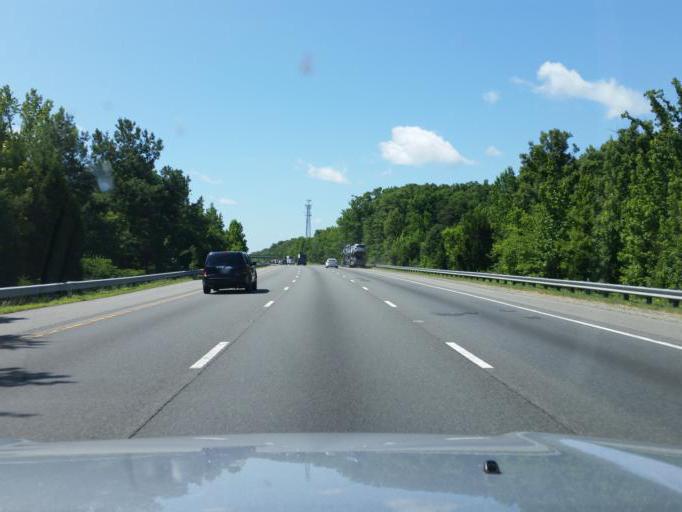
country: US
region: Virginia
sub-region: Spotsylvania County
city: Spotsylvania Courthouse
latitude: 38.2013
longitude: -77.5000
